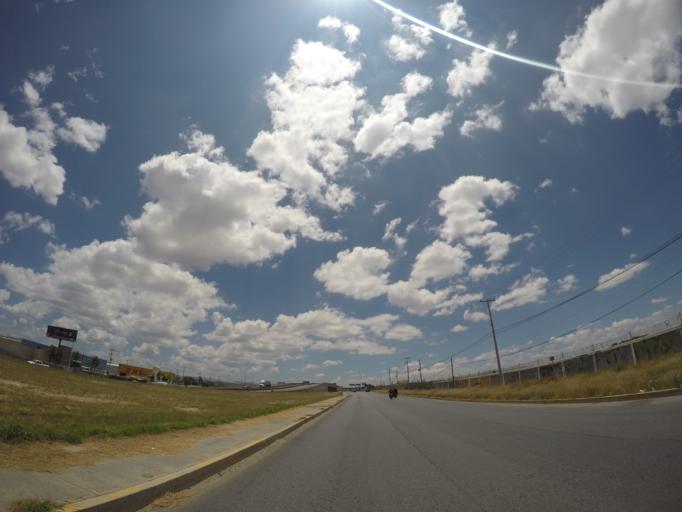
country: MX
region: San Luis Potosi
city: La Pila
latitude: 22.0453
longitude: -100.8579
